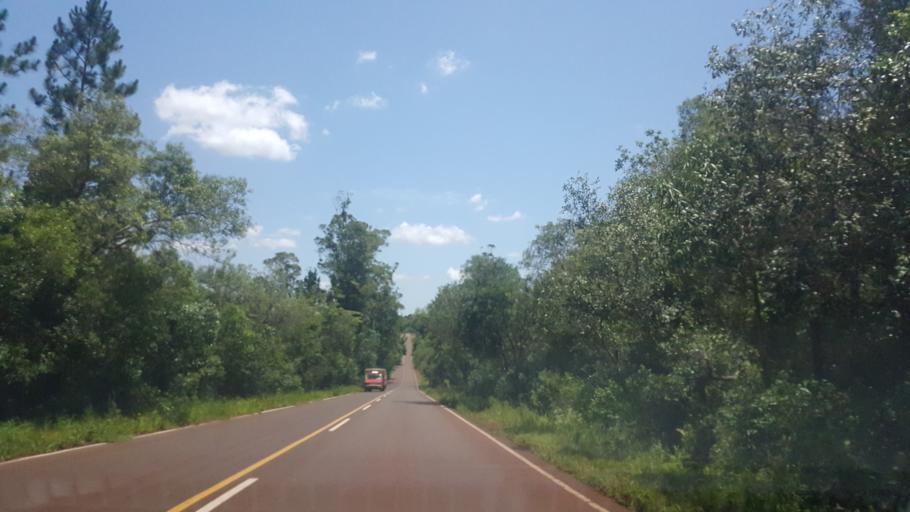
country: AR
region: Misiones
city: Garupa
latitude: -27.5032
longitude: -55.8517
